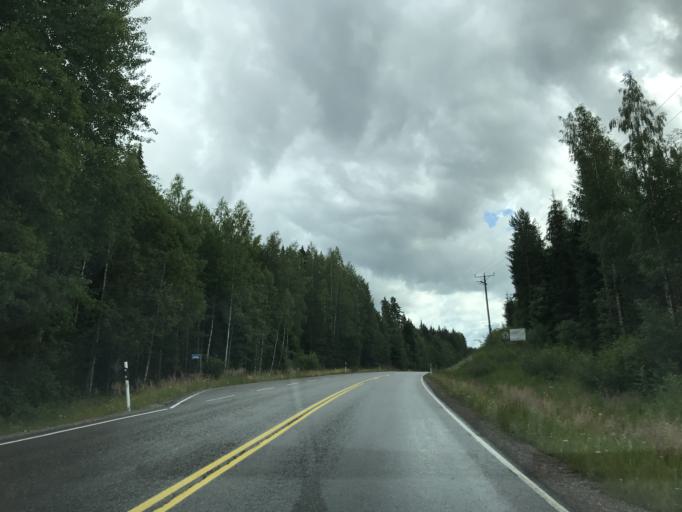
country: FI
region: Uusimaa
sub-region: Porvoo
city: Pukkila
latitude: 60.7696
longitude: 25.4972
